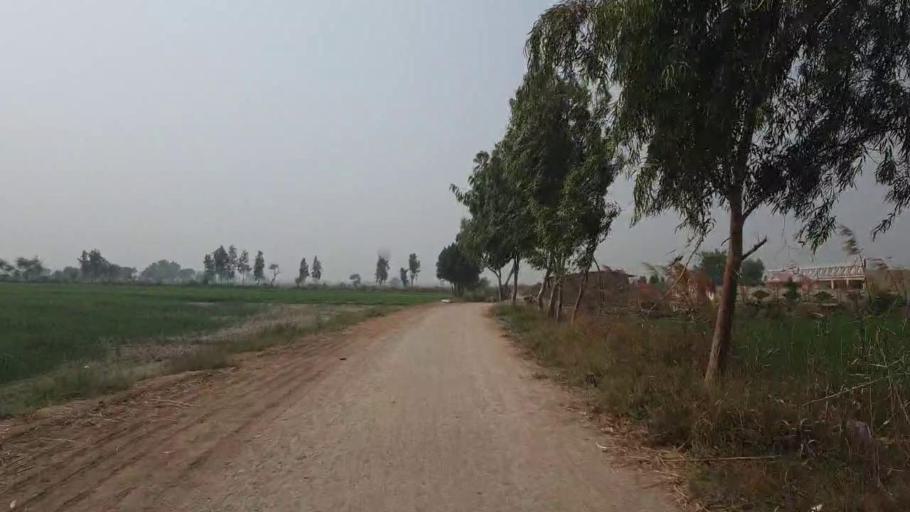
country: PK
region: Sindh
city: Kario
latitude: 24.6710
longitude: 68.6033
